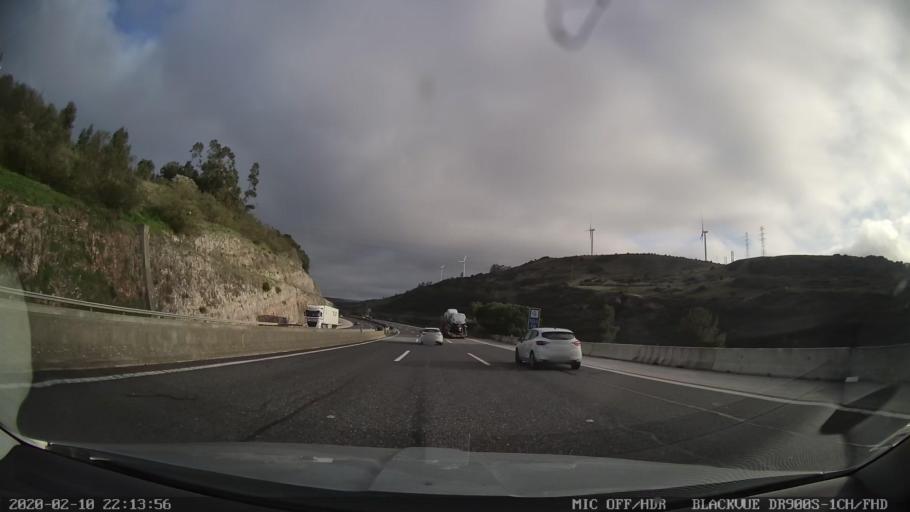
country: PT
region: Lisbon
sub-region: Loures
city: Bucelas
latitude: 38.8777
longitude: -9.1312
